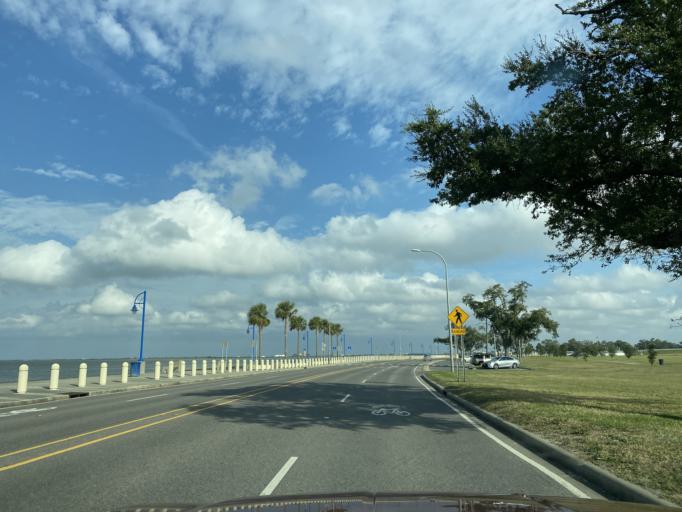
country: US
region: Louisiana
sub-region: Orleans Parish
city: New Orleans
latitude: 30.0352
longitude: -90.0472
